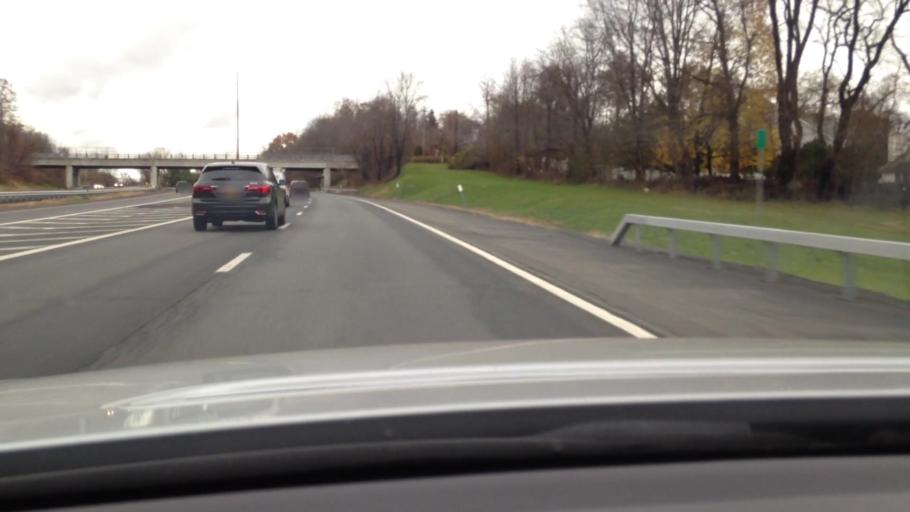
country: US
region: New York
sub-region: Rockland County
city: Chestnut Ridge
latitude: 41.0903
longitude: -74.0402
